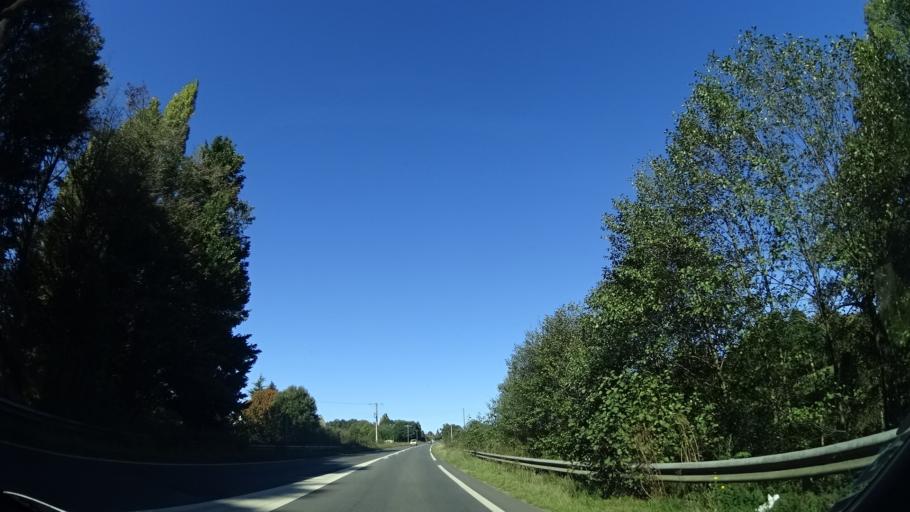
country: FR
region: Brittany
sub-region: Departement d'Ille-et-Vilaine
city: Melesse
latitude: 48.1858
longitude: -1.6937
